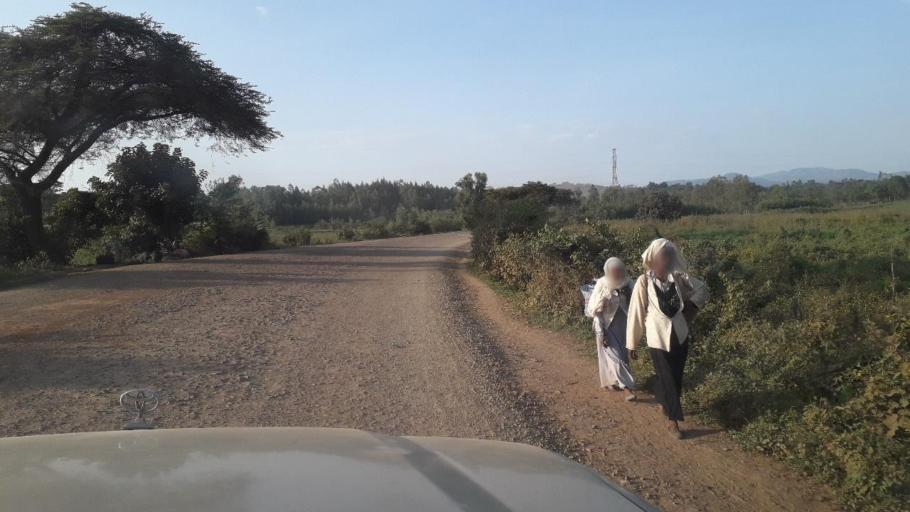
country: ET
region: Oromiya
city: Jima
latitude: 7.6146
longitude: 36.8340
